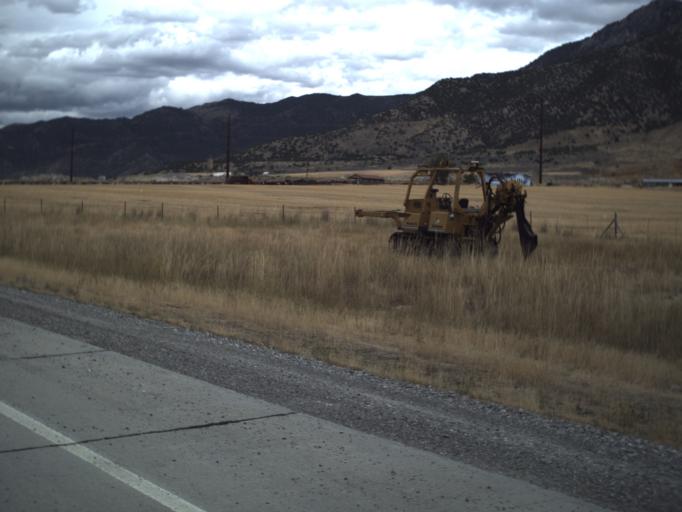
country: US
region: Utah
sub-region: Box Elder County
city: Garland
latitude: 41.8873
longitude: -112.1691
